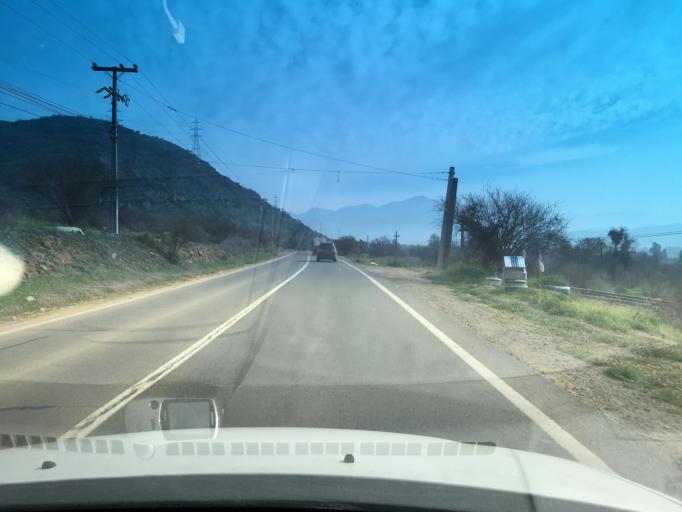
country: CL
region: Santiago Metropolitan
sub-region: Provincia de Chacabuco
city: Lampa
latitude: -33.1447
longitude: -70.9139
